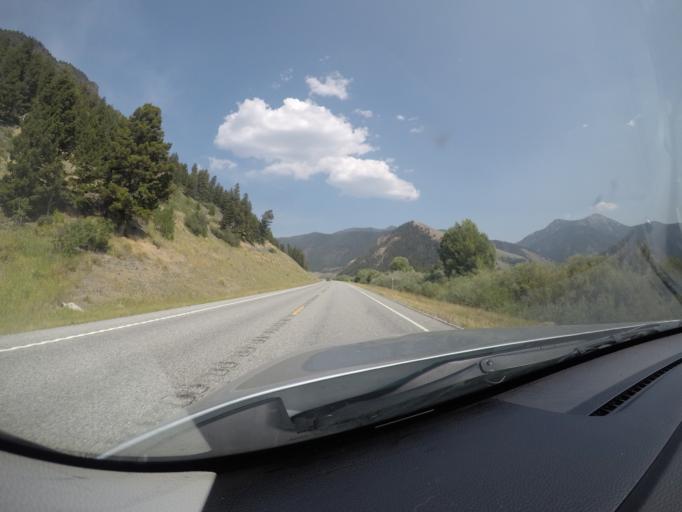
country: US
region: Montana
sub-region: Gallatin County
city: West Yellowstone
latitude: 44.8265
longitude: -111.4530
